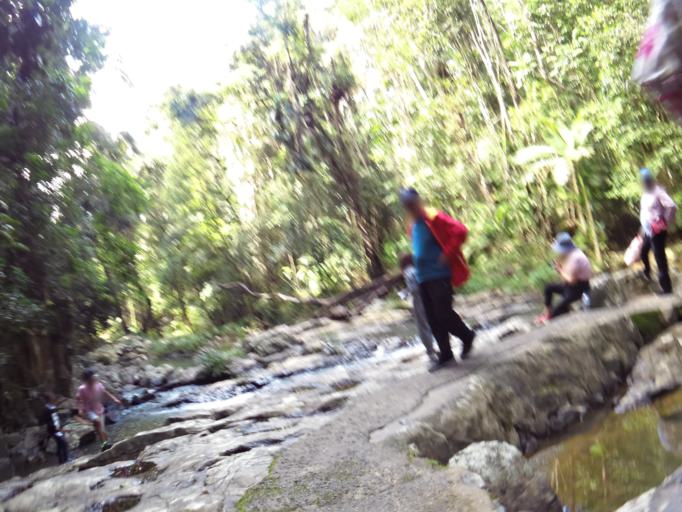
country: AU
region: Queensland
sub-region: Tablelands
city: Kuranda
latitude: -16.8251
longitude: 145.6332
